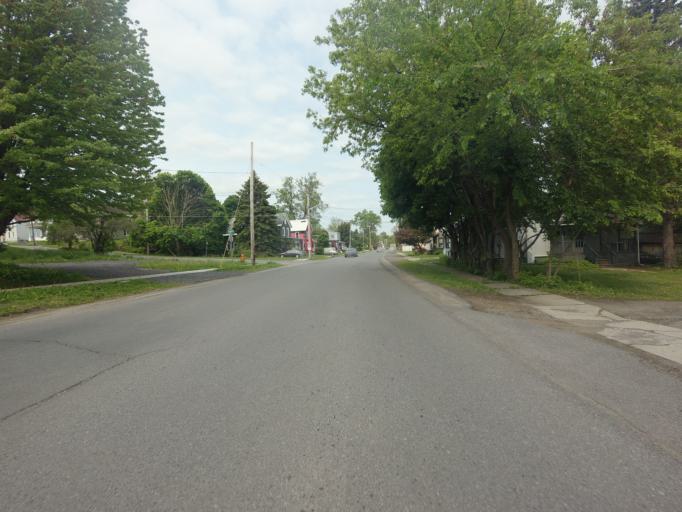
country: US
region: New York
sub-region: Jefferson County
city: Watertown
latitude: 43.9764
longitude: -75.8913
